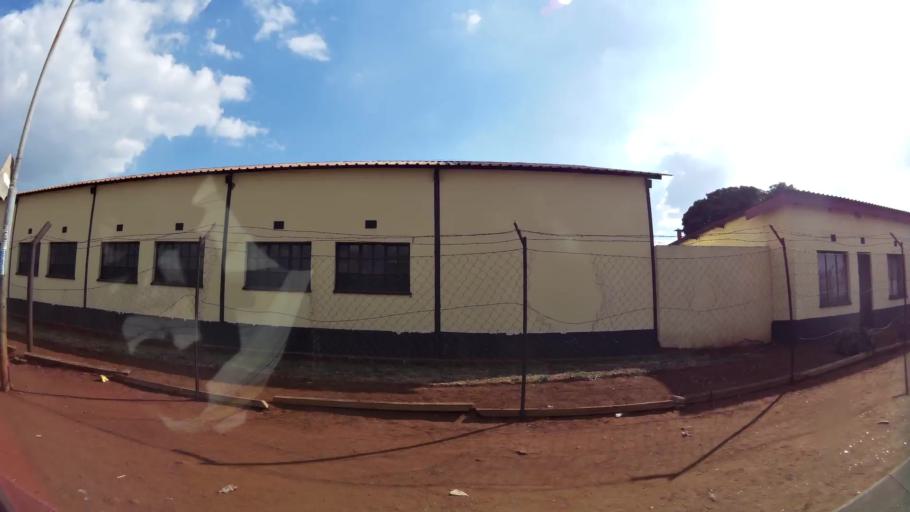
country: ZA
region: Gauteng
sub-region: City of Johannesburg Metropolitan Municipality
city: Soweto
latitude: -26.2167
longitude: 27.8607
